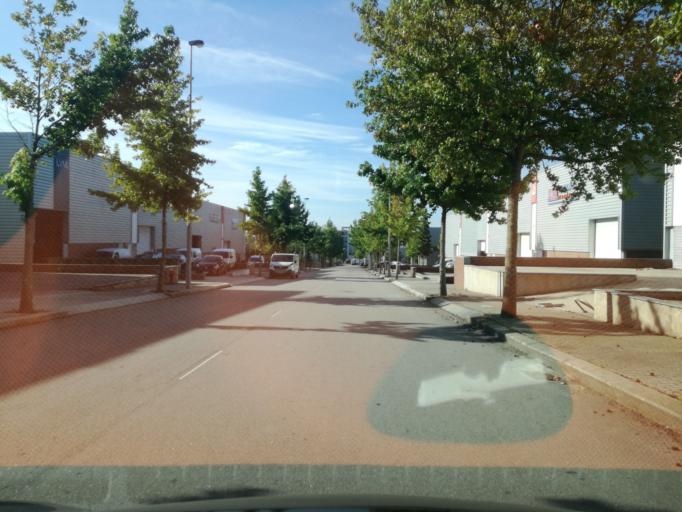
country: PT
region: Porto
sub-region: Maia
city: Anta
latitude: 41.2761
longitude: -8.6050
